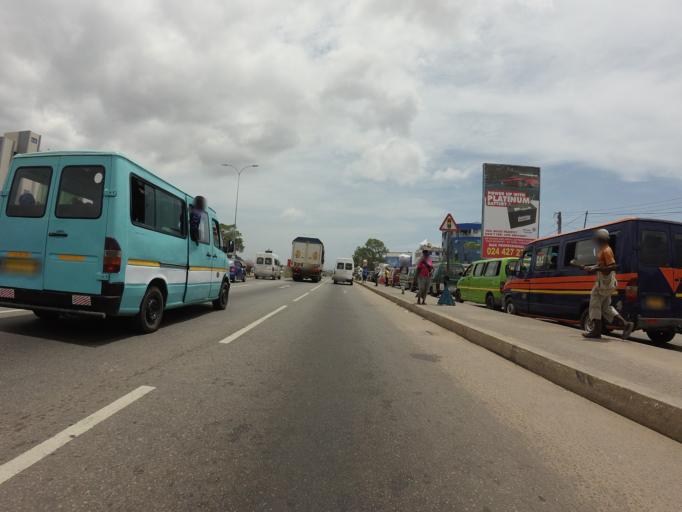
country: GH
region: Greater Accra
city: Gbawe
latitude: 5.5754
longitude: -0.2531
